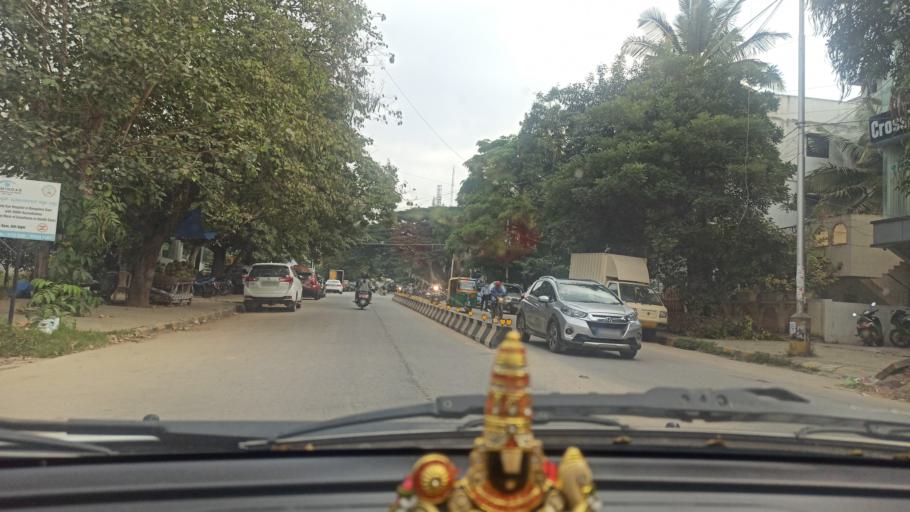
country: IN
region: Karnataka
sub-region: Bangalore Urban
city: Bangalore
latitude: 13.0148
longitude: 77.6464
